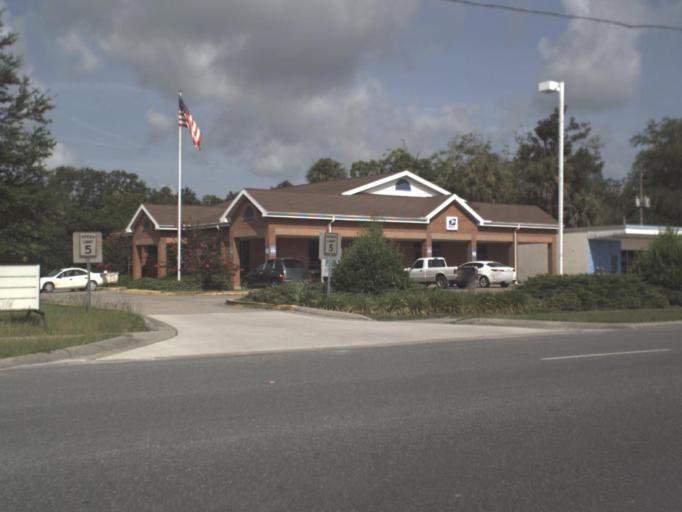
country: US
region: Florida
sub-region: Lafayette County
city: Mayo
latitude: 29.9591
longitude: -82.9291
